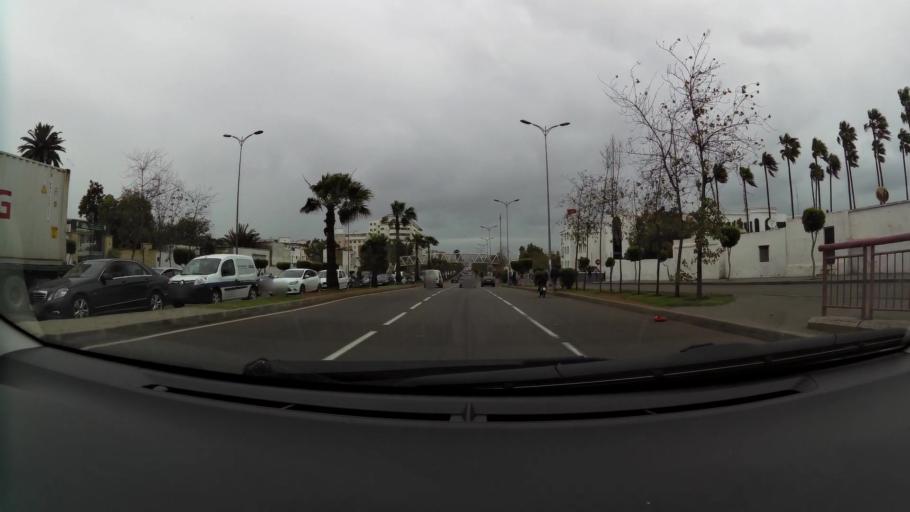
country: MA
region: Grand Casablanca
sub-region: Casablanca
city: Casablanca
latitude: 33.5793
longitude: -7.5902
